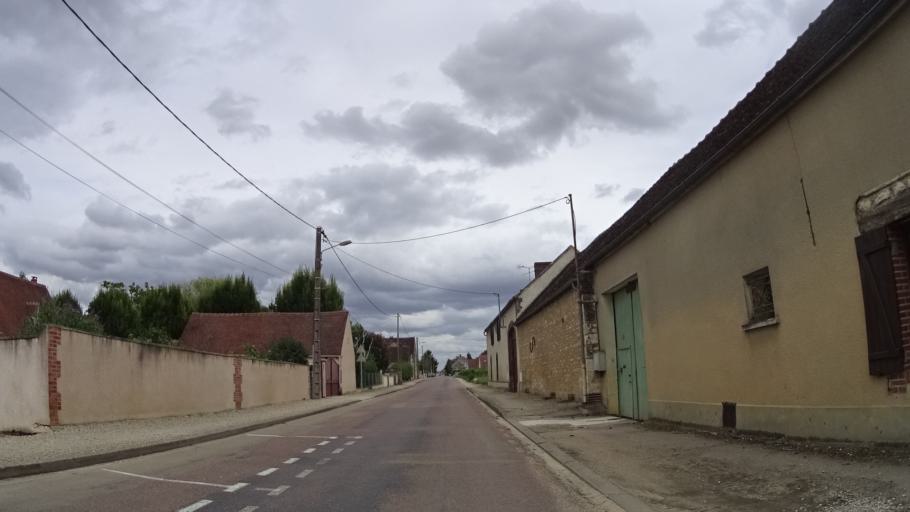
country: FR
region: Bourgogne
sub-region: Departement de l'Yonne
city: Joigny
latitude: 47.9539
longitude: 3.4061
